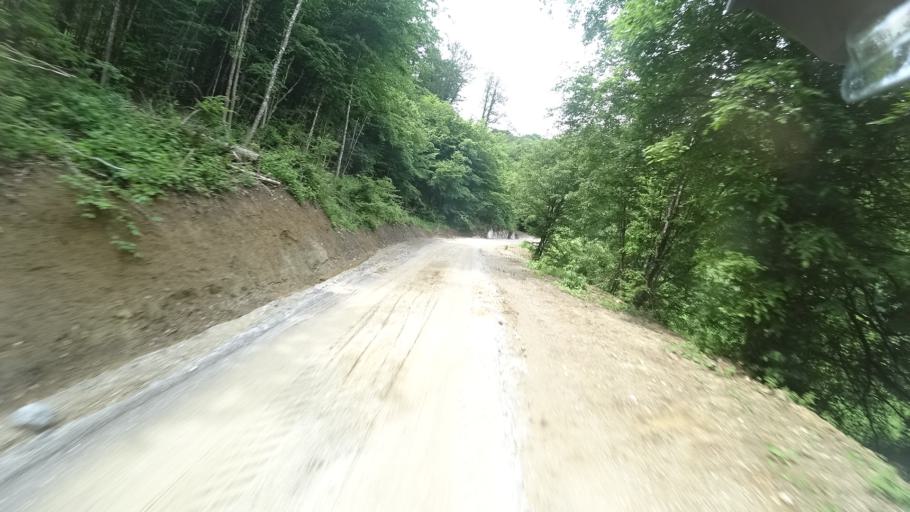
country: HR
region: Karlovacka
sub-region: Grad Karlovac
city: Slunj
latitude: 45.2114
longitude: 15.6307
